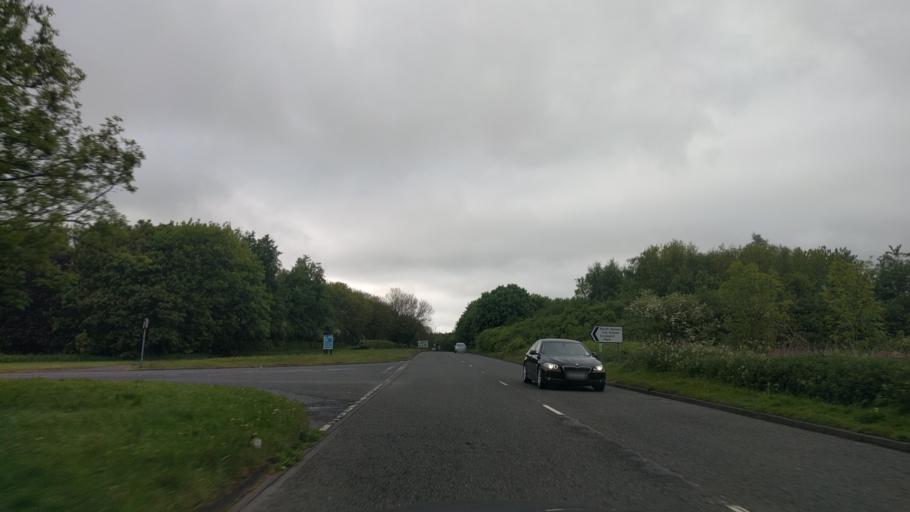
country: GB
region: England
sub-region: Northumberland
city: Cramlington
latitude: 55.0989
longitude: -1.5952
